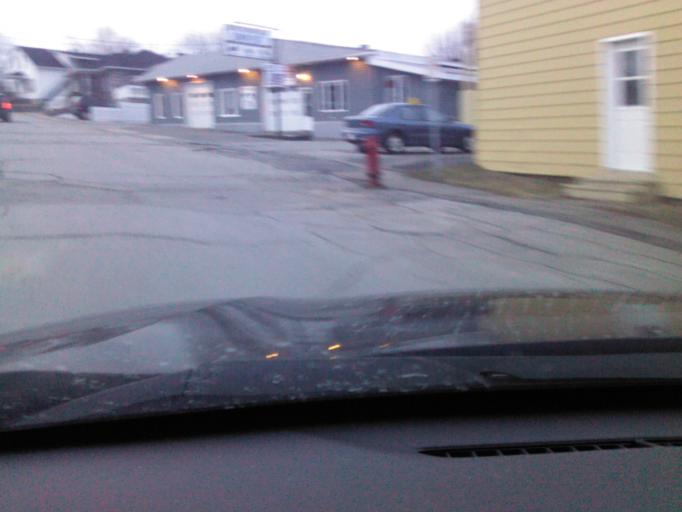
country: CA
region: Quebec
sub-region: Capitale-Nationale
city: Donnacona
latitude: 46.6733
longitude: -71.7343
